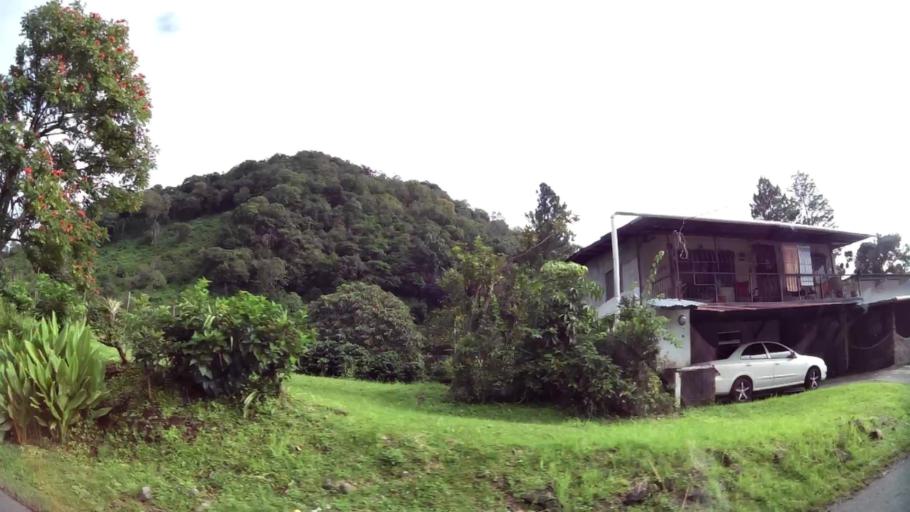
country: PA
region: Chiriqui
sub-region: Distrito Boquete
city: Boquete
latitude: 8.7965
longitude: -82.4487
